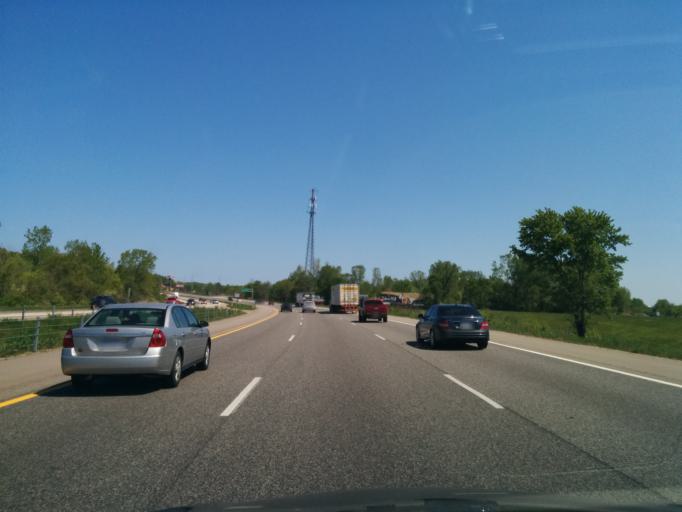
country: US
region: Michigan
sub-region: Berrien County
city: Bridgman
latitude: 41.9228
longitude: -86.5703
